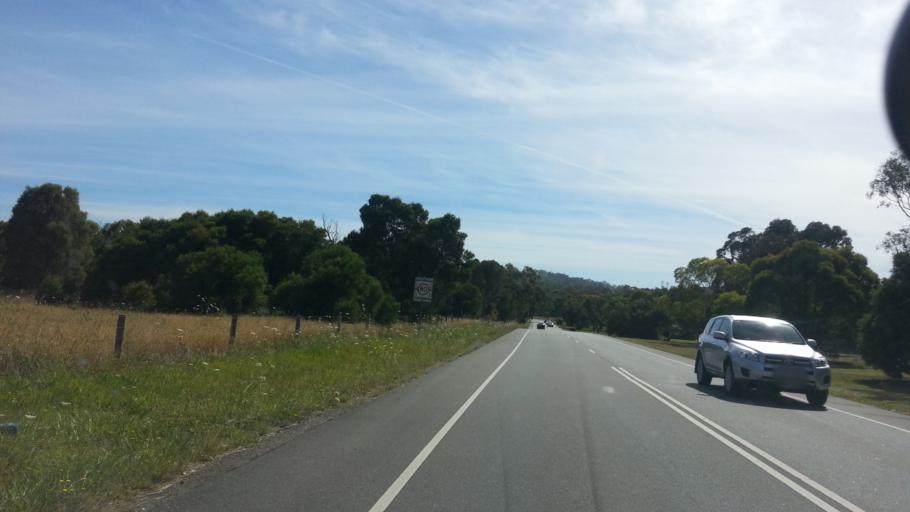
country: AU
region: Victoria
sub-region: Casey
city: Endeavour Hills
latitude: -37.9645
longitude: 145.2448
